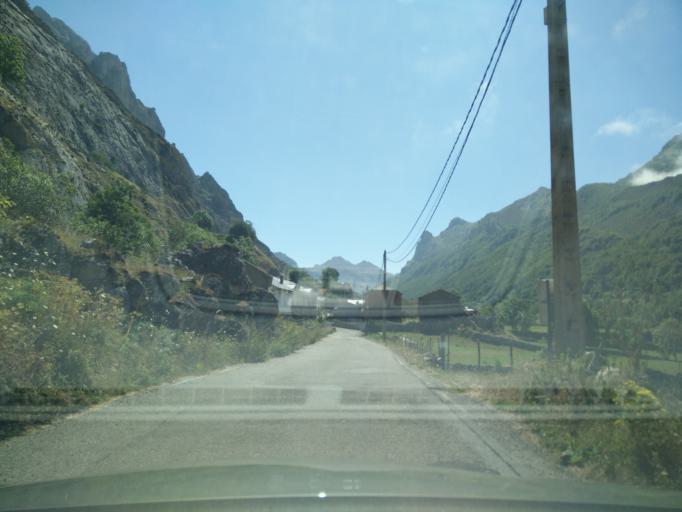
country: ES
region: Asturias
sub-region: Province of Asturias
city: Pola de Somiedo
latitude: 43.0735
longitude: -6.2018
